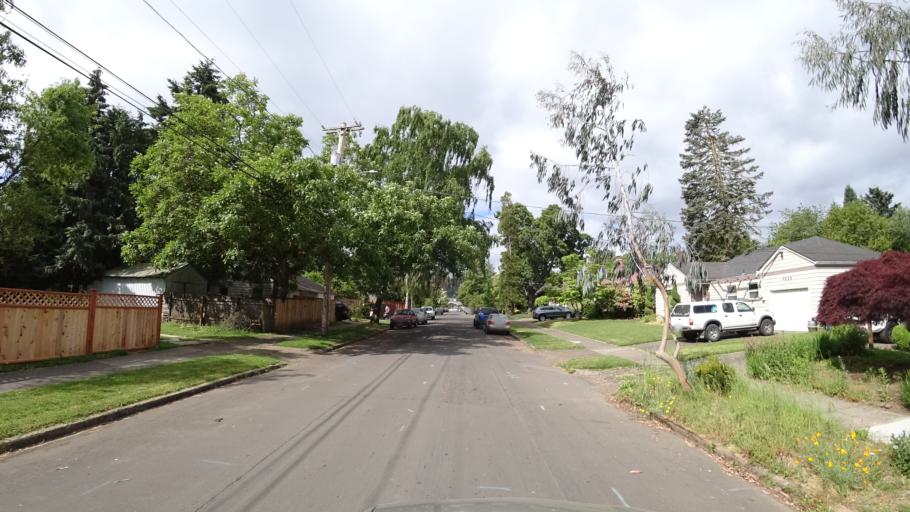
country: US
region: Oregon
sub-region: Washington County
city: West Haven
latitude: 45.5959
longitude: -122.7549
